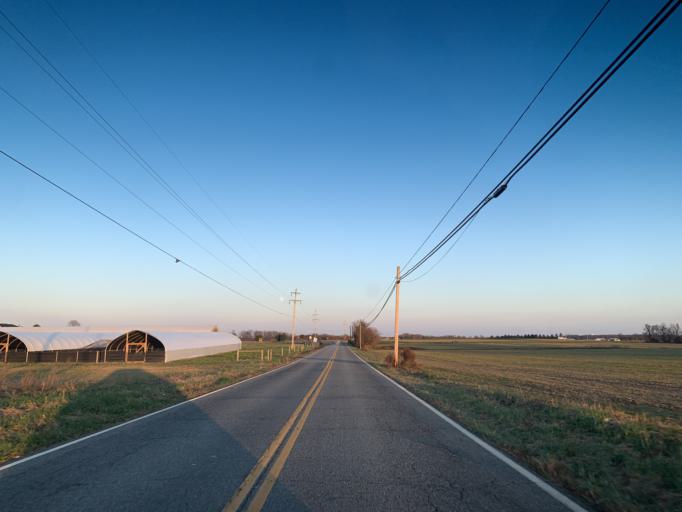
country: US
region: Maryland
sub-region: Cecil County
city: Charlestown
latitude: 39.4107
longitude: -75.9145
